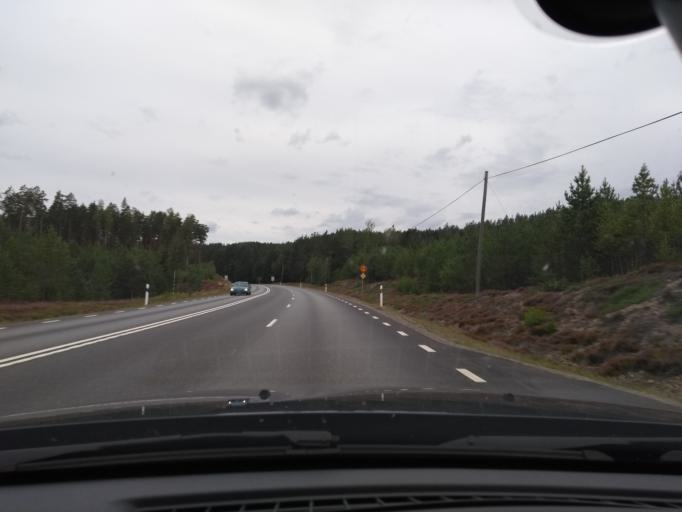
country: SE
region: Joenkoeping
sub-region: Eksjo Kommun
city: Haljarp
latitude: 57.6382
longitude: 15.3151
